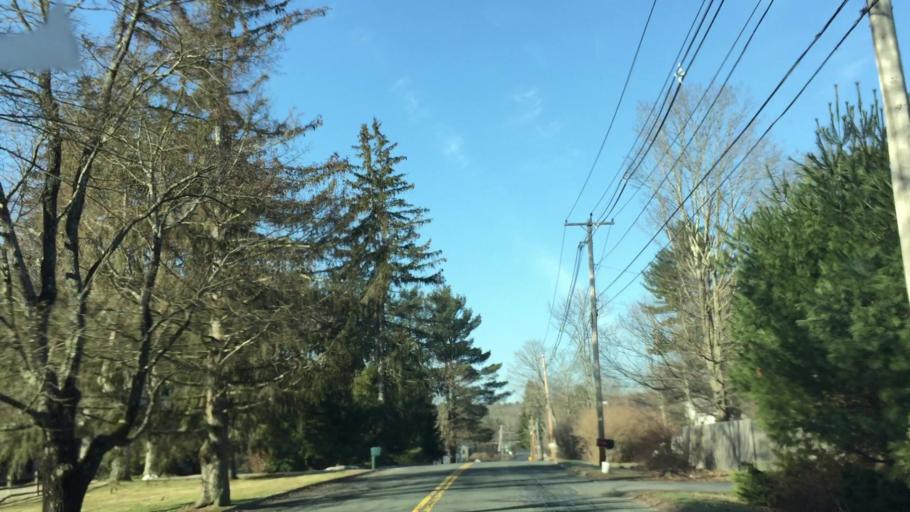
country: US
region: Massachusetts
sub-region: Berkshire County
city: Housatonic
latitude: 42.2301
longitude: -73.3599
